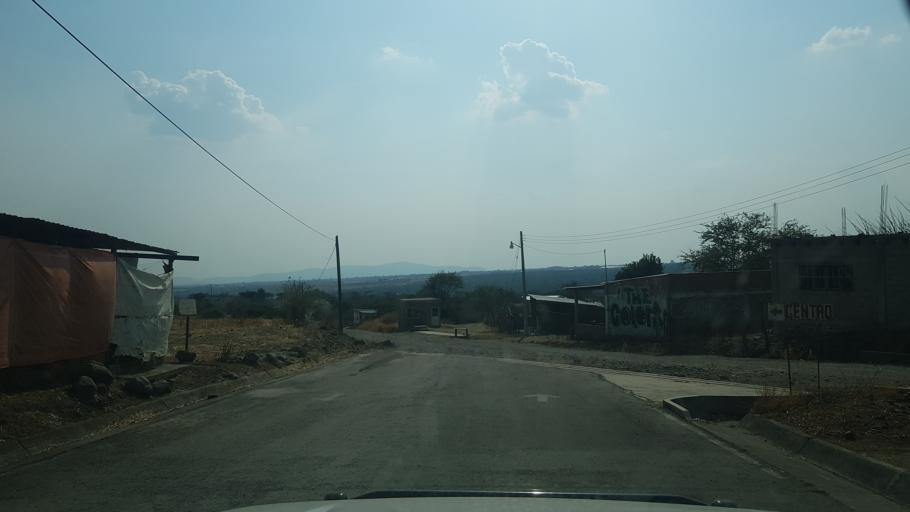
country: MX
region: Morelos
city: Tlacotepec
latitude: 18.7795
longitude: -98.7250
